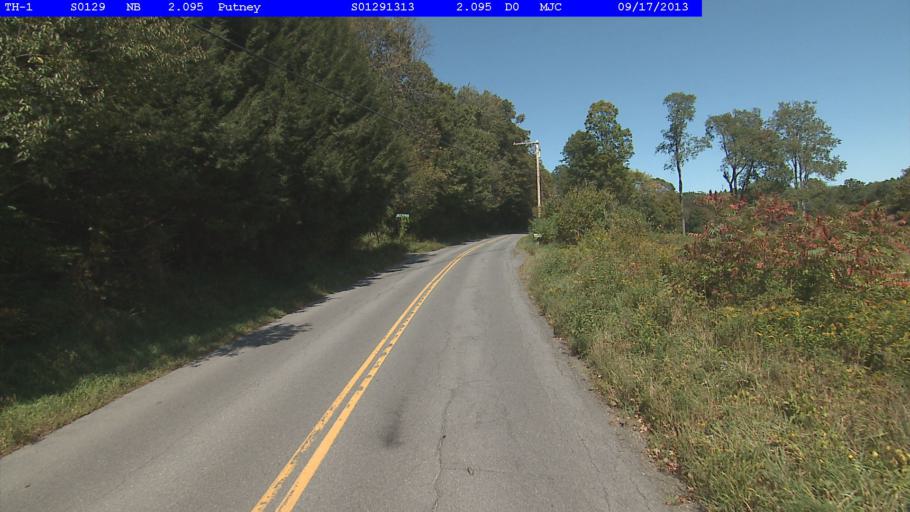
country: US
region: New Hampshire
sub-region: Cheshire County
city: Westmoreland
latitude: 43.0028
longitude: -72.5327
